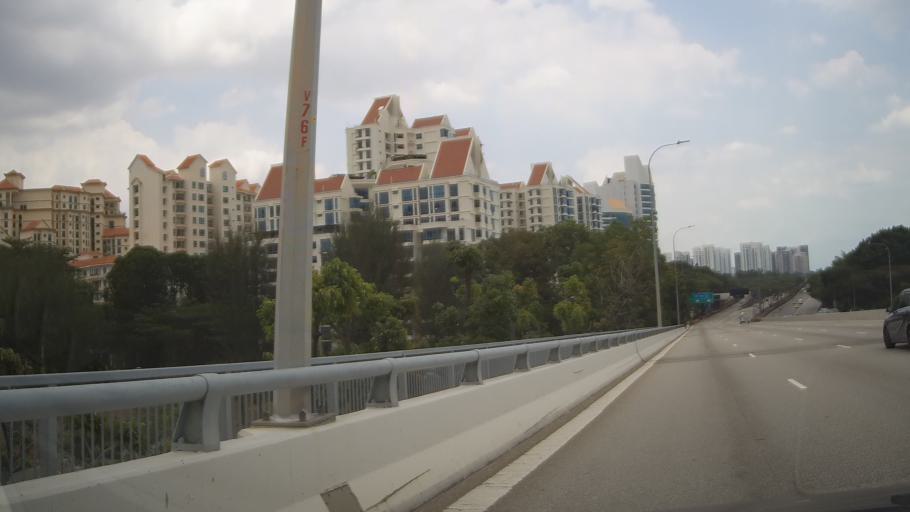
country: SG
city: Singapore
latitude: 1.2952
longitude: 103.8688
